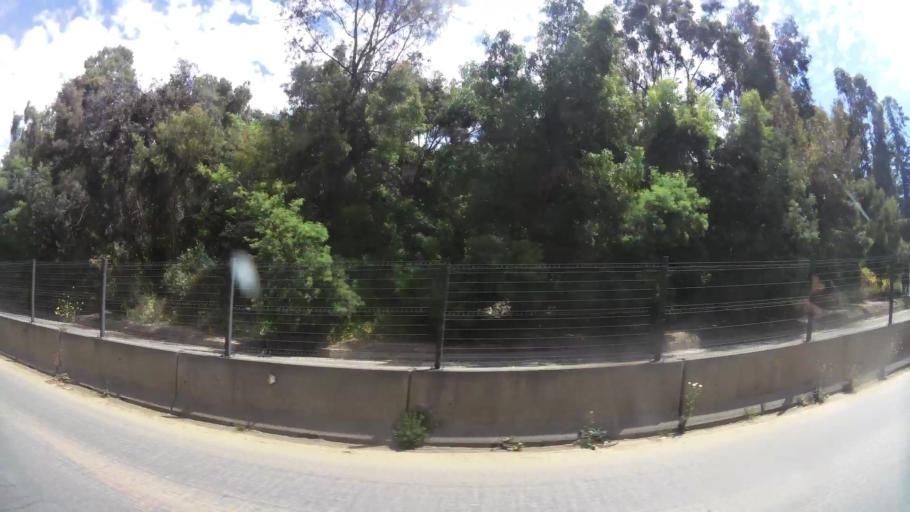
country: CL
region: Valparaiso
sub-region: Provincia de Valparaiso
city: Vina del Mar
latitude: -33.0544
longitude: -71.5844
